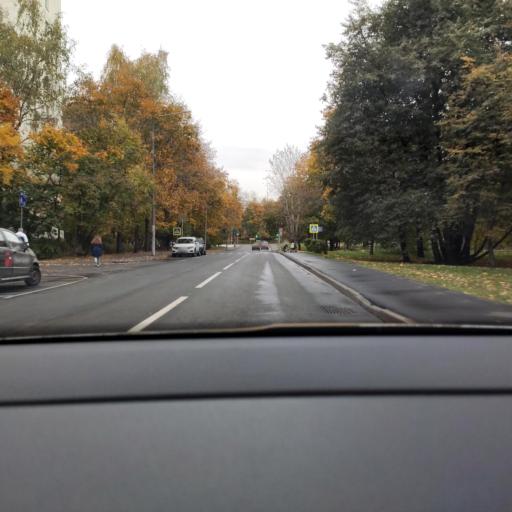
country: RU
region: Moscow
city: Leonovo
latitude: 55.8574
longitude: 37.6699
